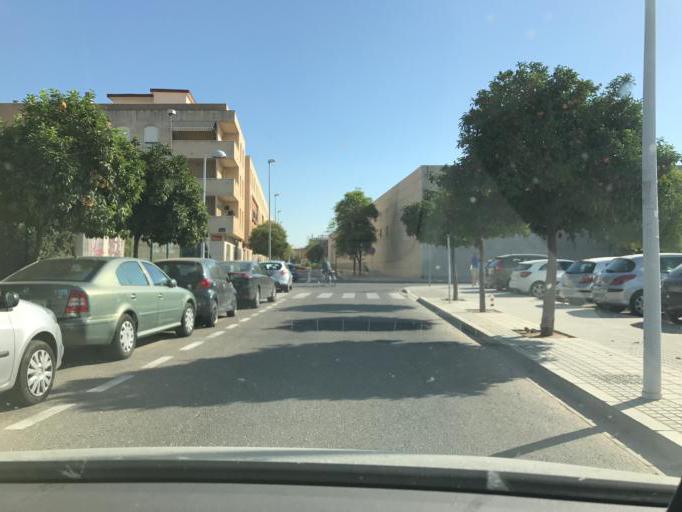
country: ES
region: Andalusia
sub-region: Province of Cordoba
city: Cordoba
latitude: 37.8894
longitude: -4.7916
